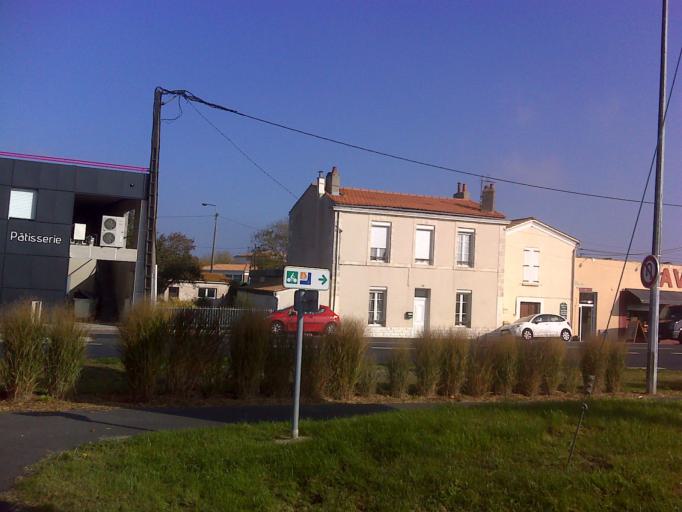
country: FR
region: Poitou-Charentes
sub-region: Departement de la Charente-Maritime
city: Breuil-Magne
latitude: 45.9503
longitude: -0.9440
